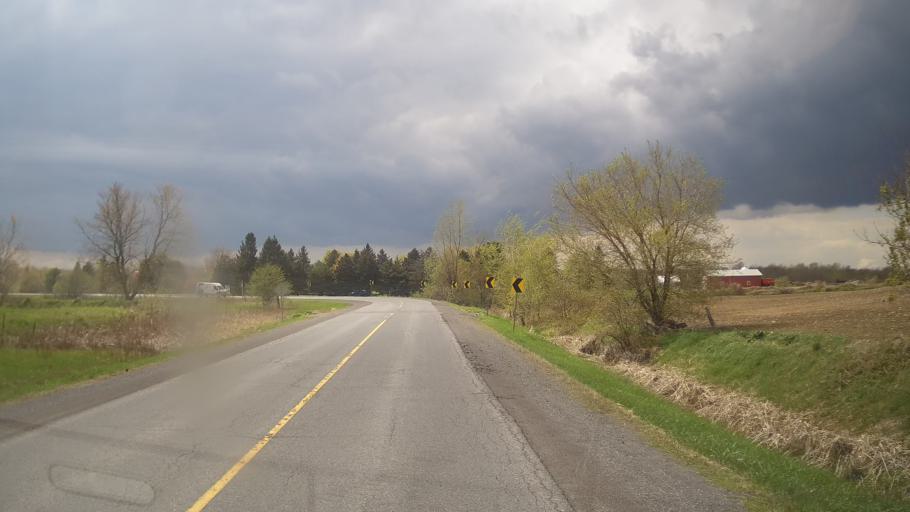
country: CA
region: Ontario
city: Hawkesbury
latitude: 45.5189
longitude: -74.5684
